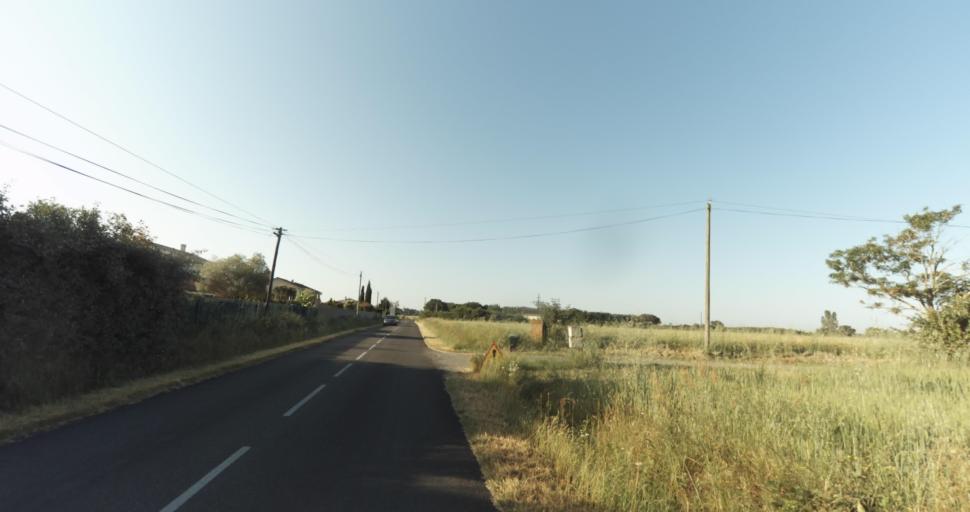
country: FR
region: Midi-Pyrenees
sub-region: Departement de la Haute-Garonne
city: Leguevin
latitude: 43.5898
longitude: 1.2363
